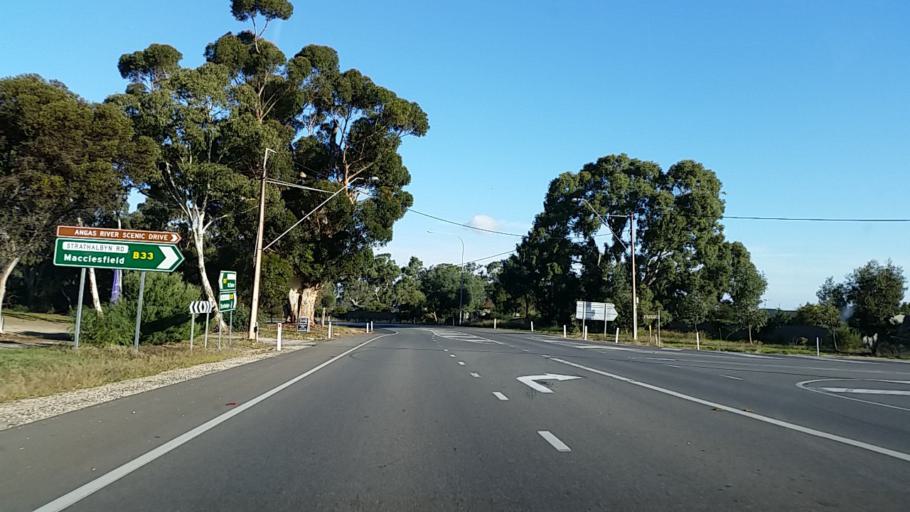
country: AU
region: South Australia
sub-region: Alexandrina
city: Strathalbyn
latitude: -35.2423
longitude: 138.8941
